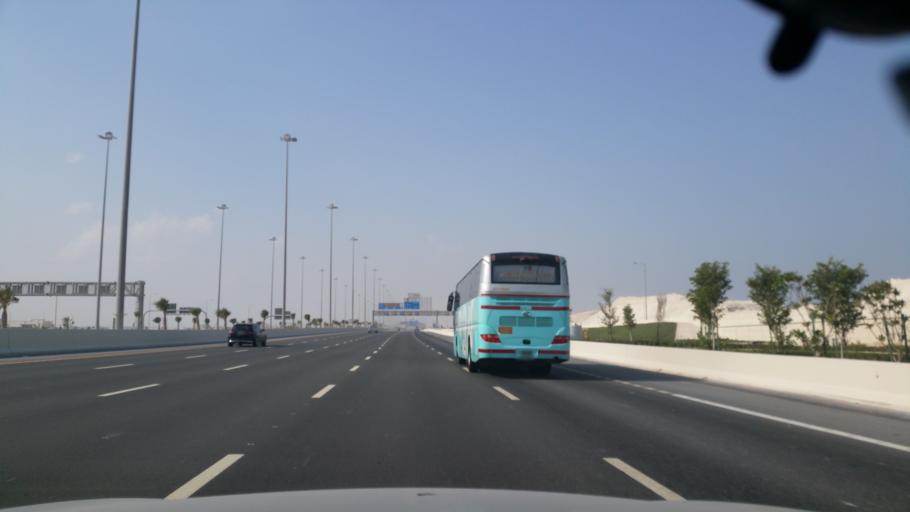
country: QA
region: Baladiyat Umm Salal
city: Umm Salal Muhammad
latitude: 25.4321
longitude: 51.4841
